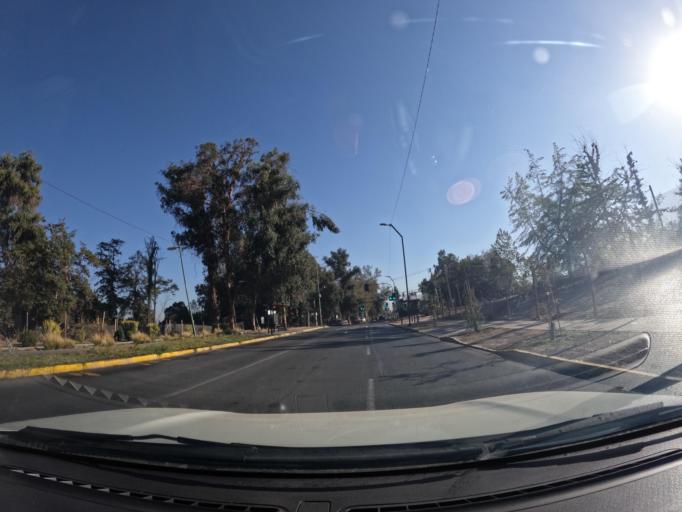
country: CL
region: Santiago Metropolitan
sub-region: Provincia de Santiago
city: Villa Presidente Frei, Nunoa, Santiago, Chile
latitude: -33.5019
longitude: -70.5434
